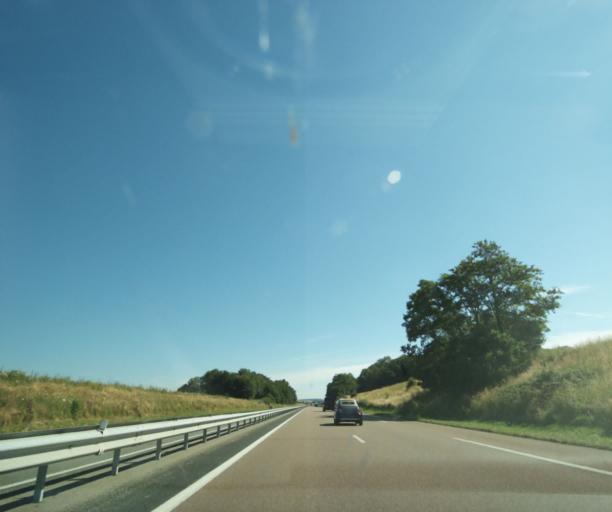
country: FR
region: Champagne-Ardenne
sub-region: Departement de la Haute-Marne
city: Saulxures
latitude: 48.0687
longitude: 5.5933
